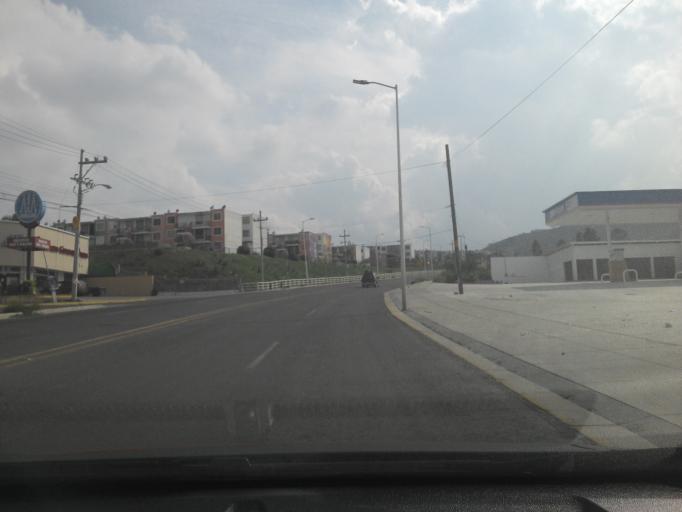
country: MX
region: Jalisco
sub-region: Tlajomulco de Zuniga
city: Lomas del Sur
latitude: 20.4933
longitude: -103.4180
